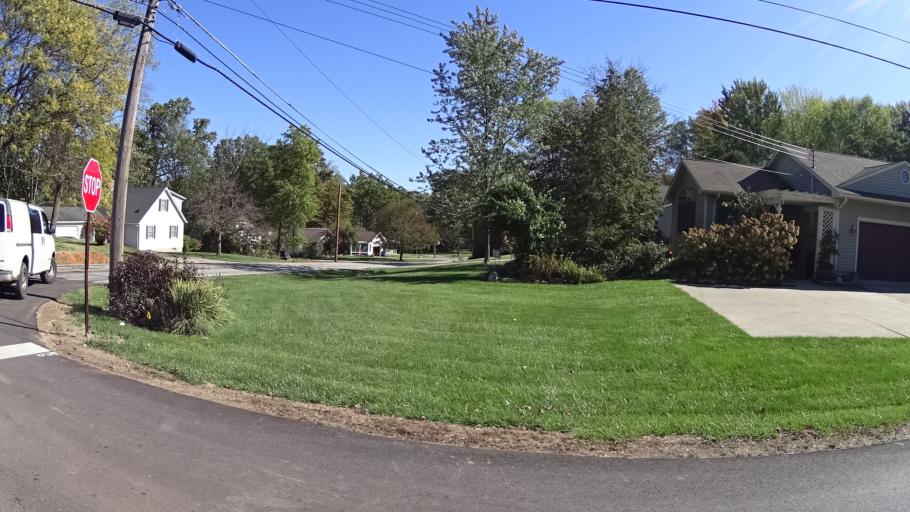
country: US
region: Ohio
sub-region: Lorain County
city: Amherst
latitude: 41.4022
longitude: -82.2368
